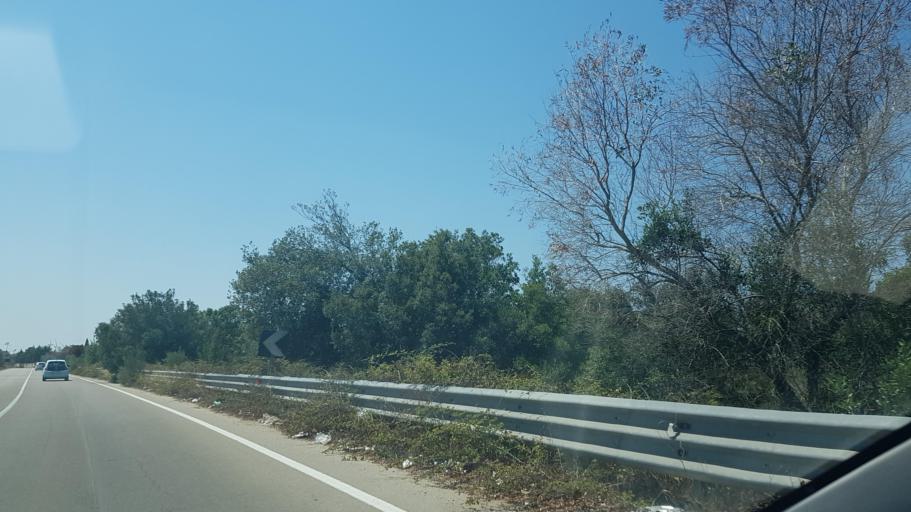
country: IT
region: Apulia
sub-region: Provincia di Lecce
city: Vernole
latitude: 40.2904
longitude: 18.3175
